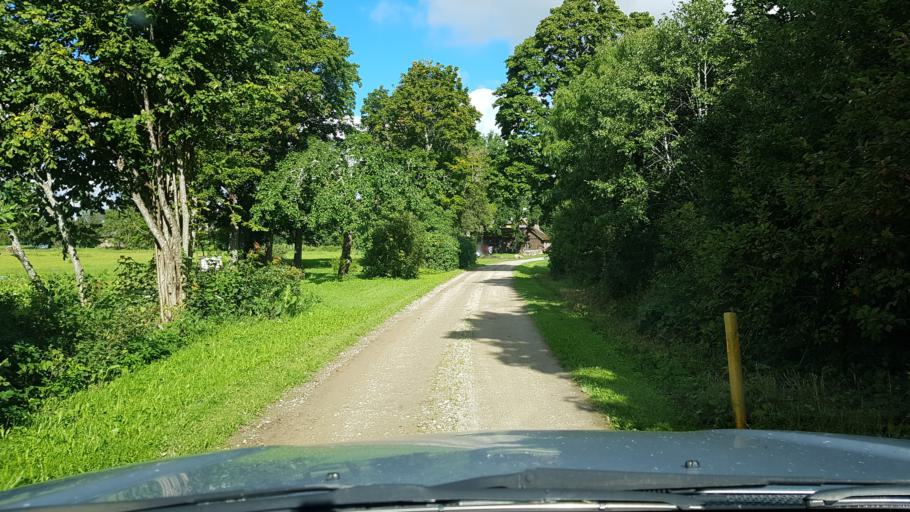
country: EE
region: Harju
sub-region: Raasiku vald
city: Arukula
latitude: 59.2619
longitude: 25.0964
